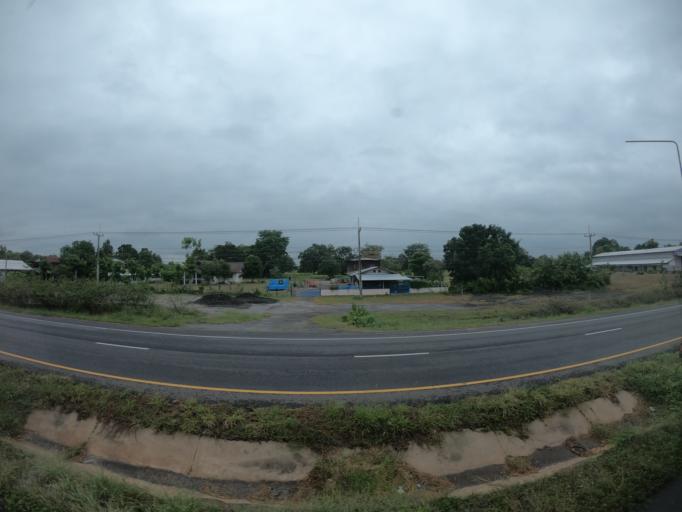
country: TH
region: Nakhon Ratchasima
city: Sida
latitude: 15.5844
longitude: 102.5571
